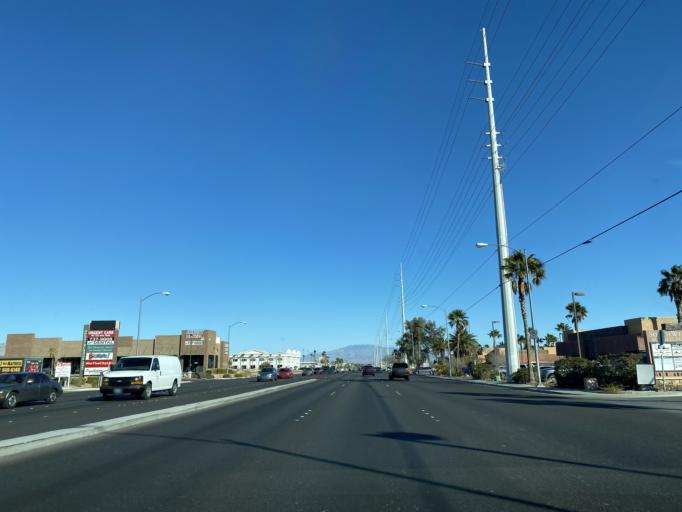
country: US
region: Nevada
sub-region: Clark County
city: Spring Valley
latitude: 36.0787
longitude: -115.2426
